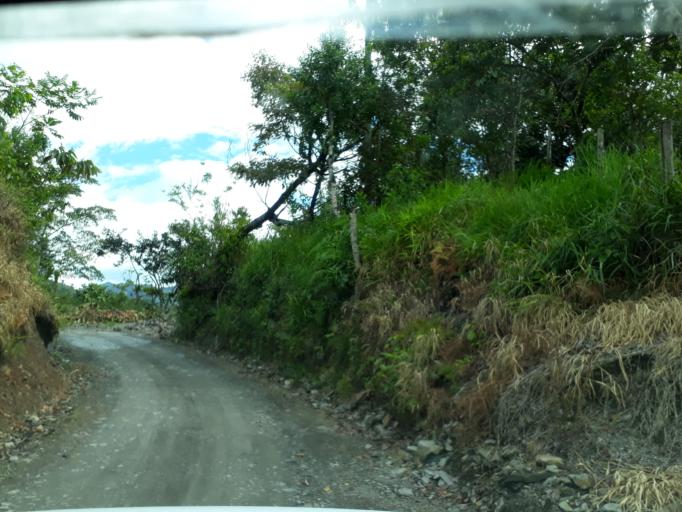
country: CO
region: Boyaca
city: Quipama
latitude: 5.4451
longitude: -74.1808
